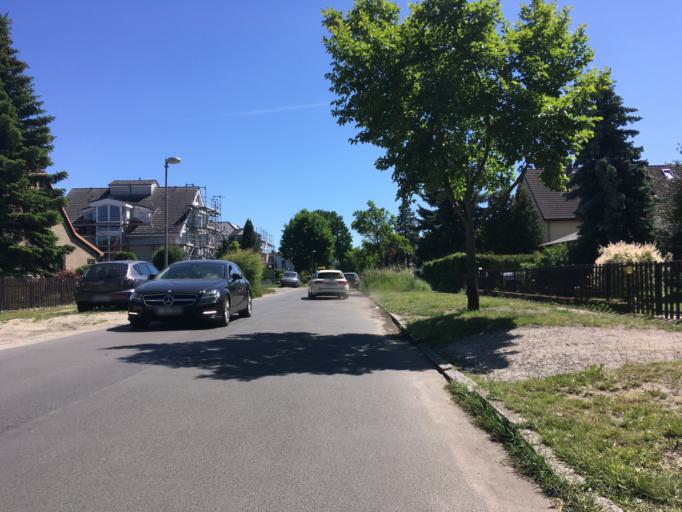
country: DE
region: Berlin
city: Berlin Koepenick
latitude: 52.4331
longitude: 13.5912
